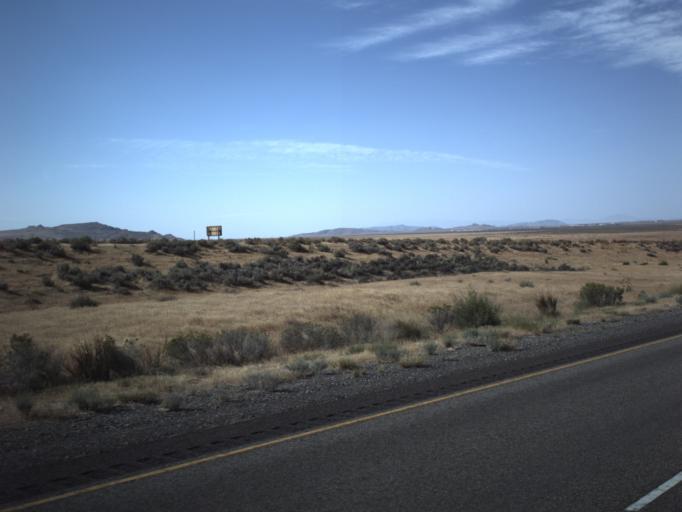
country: US
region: Utah
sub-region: Tooele County
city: Grantsville
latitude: 40.7570
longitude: -113.0246
